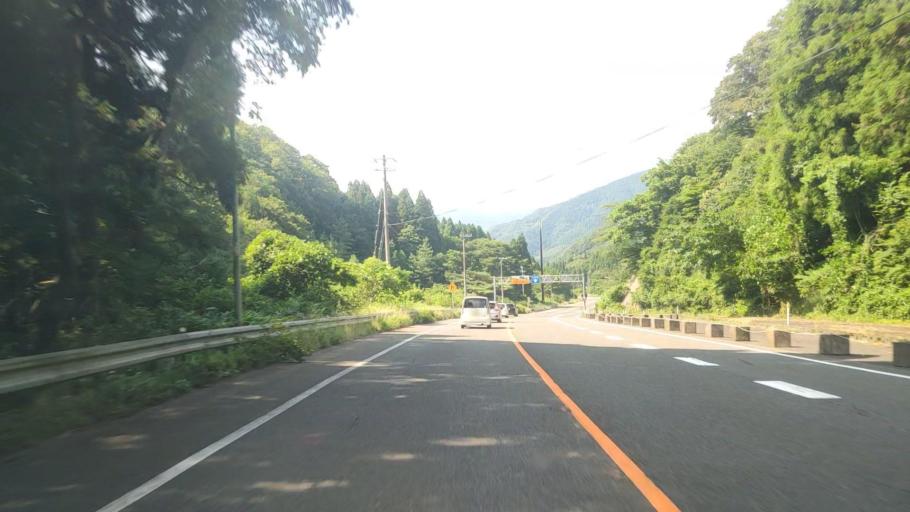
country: JP
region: Fukui
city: Tsuruga
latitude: 35.5958
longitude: 136.1228
